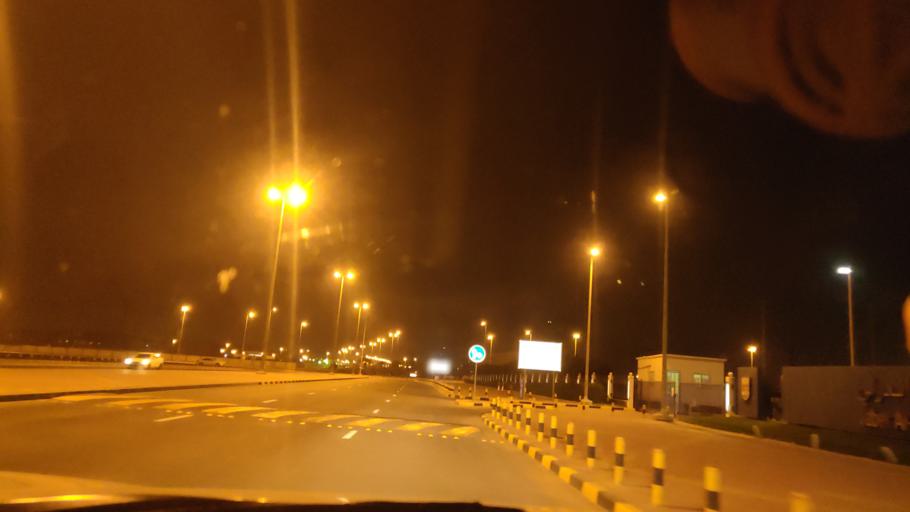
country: KW
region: Al Asimah
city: Ar Rabiyah
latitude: 29.2726
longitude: 47.9160
